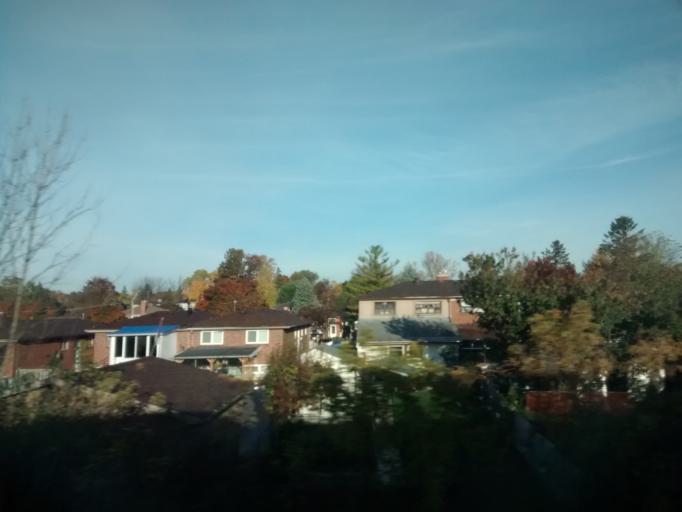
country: CA
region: Ontario
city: Etobicoke
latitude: 43.5692
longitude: -79.5727
